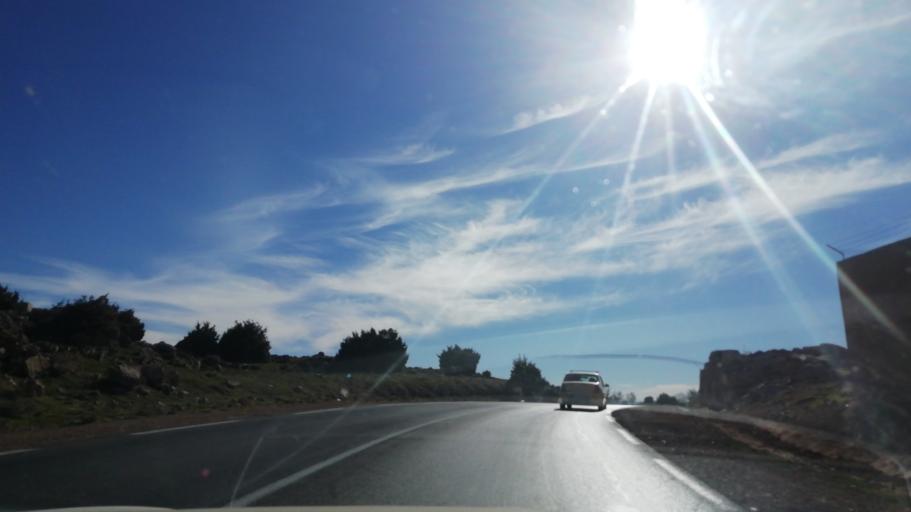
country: DZ
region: Tlemcen
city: Mansoura
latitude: 34.7533
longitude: -1.3440
